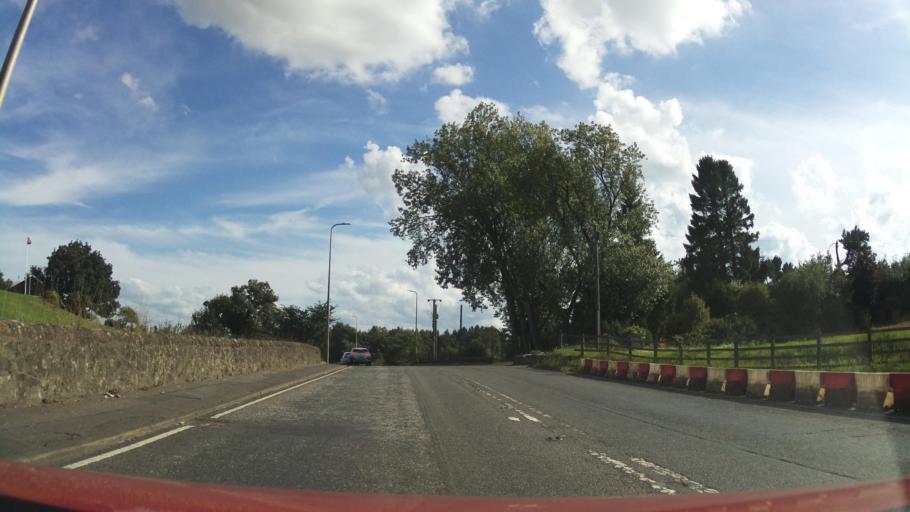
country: GB
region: Scotland
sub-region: Falkirk
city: Larbert
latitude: 56.0349
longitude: -3.8541
